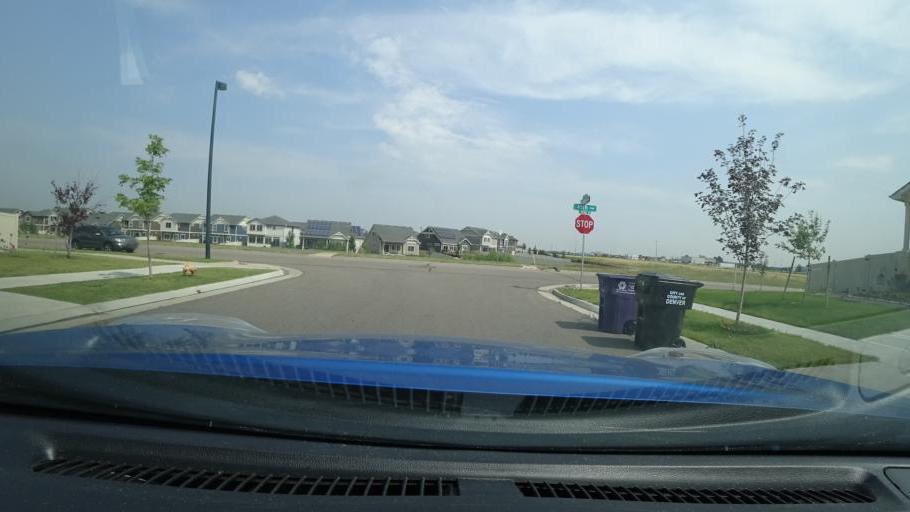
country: US
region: Colorado
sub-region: Adams County
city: Aurora
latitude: 39.7779
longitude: -104.7757
